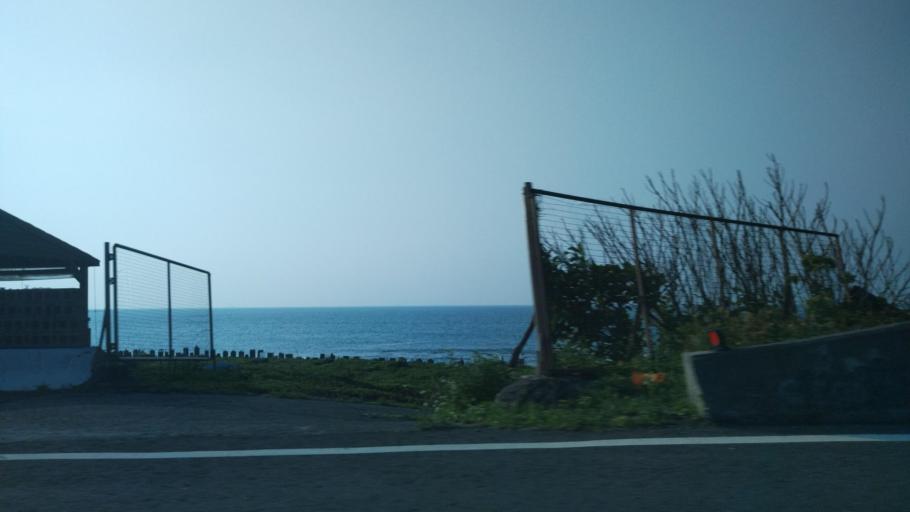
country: TW
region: Taipei
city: Taipei
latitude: 25.2918
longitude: 121.5536
